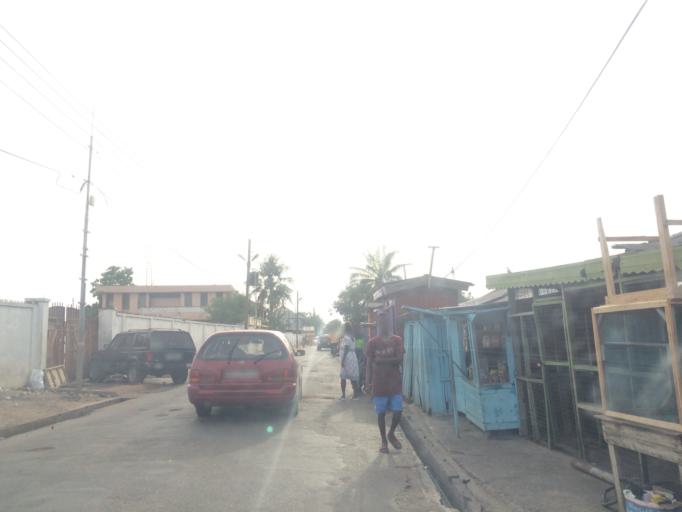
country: GH
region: Greater Accra
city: Accra
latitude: 5.5423
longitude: -0.2143
